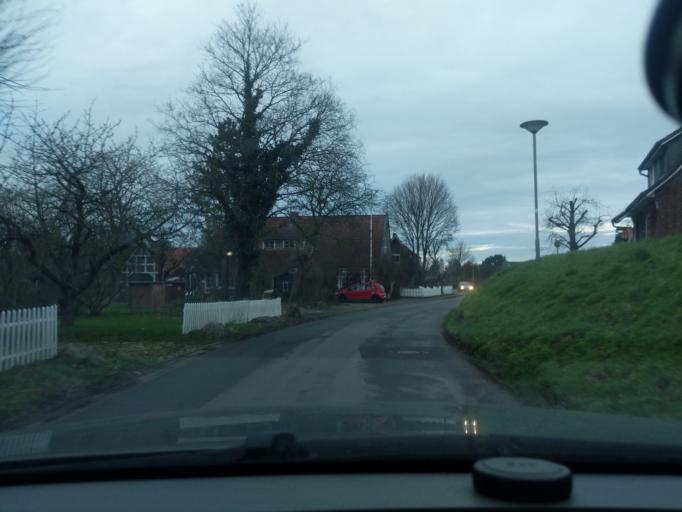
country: DE
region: Lower Saxony
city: Guderhandviertel
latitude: 53.5384
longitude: 9.6110
